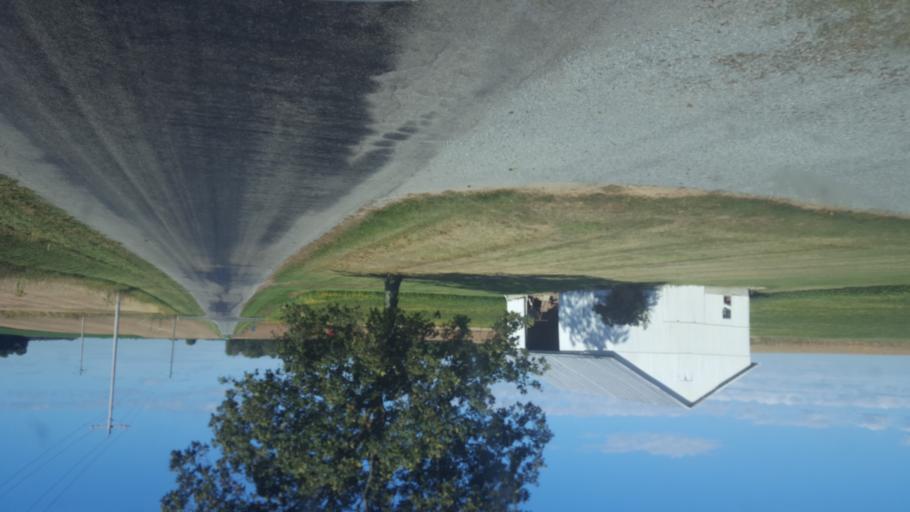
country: US
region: Ohio
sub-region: Wyandot County
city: Upper Sandusky
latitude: 40.7881
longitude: -83.2173
